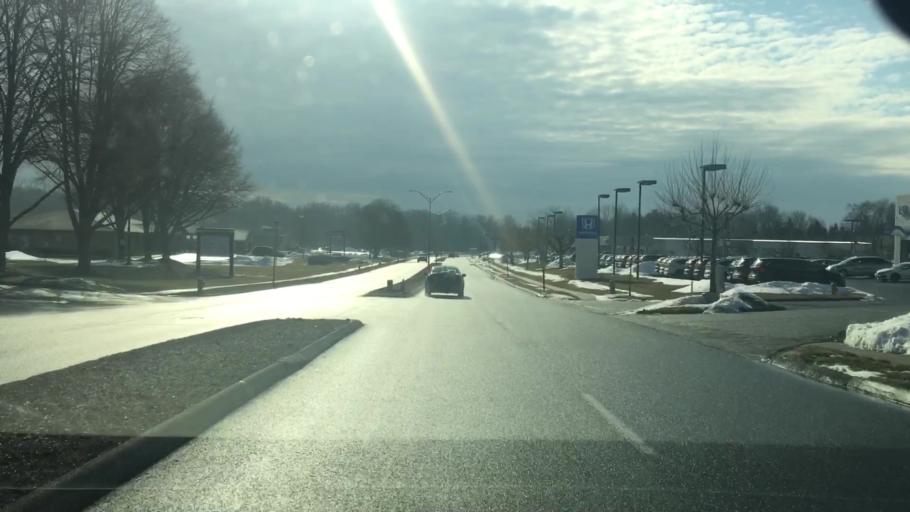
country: US
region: Connecticut
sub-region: Hartford County
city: Sherwood Manor
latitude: 41.9976
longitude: -72.5740
